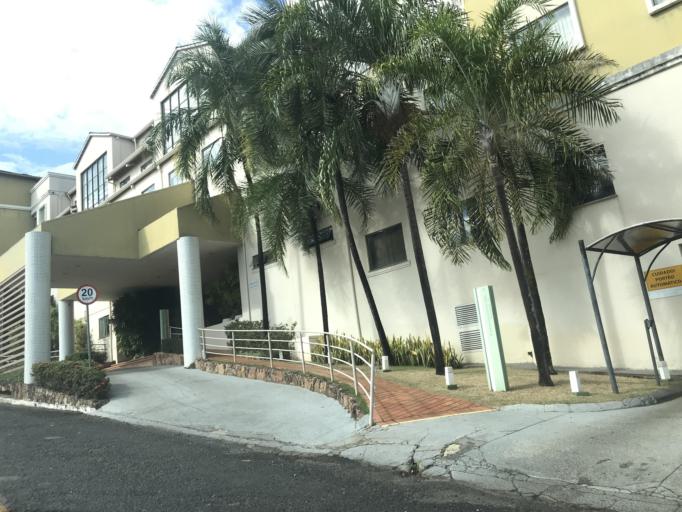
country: BR
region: Goias
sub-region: Caldas Novas
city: Caldas Novas
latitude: -17.7710
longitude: -48.7575
